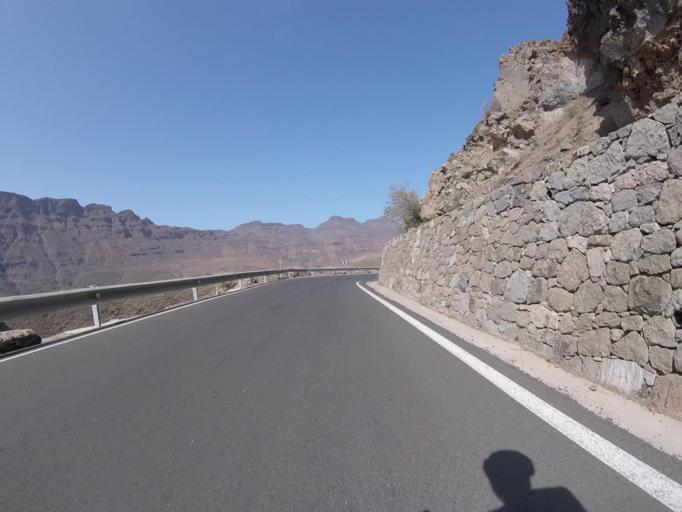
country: ES
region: Canary Islands
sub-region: Provincia de Las Palmas
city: Santa Lucia
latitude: 27.8883
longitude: -15.5258
